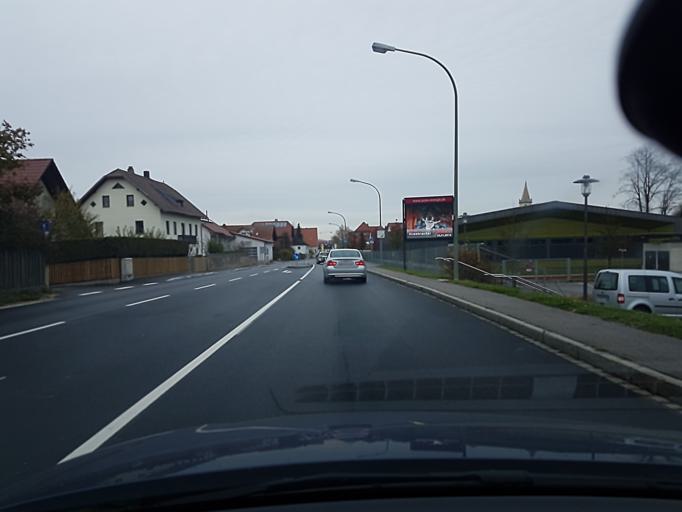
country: DE
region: Bavaria
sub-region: Lower Bavaria
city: Essenbach
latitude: 48.6098
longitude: 12.2123
